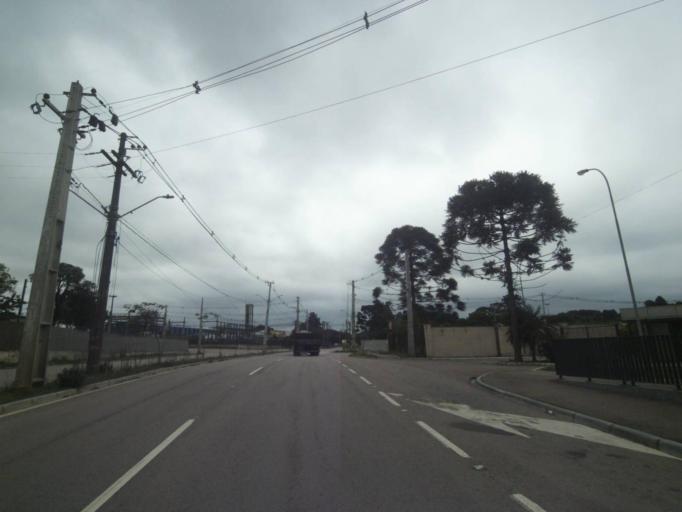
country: BR
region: Parana
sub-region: Sao Jose Dos Pinhais
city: Sao Jose dos Pinhais
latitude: -25.5546
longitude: -49.3068
